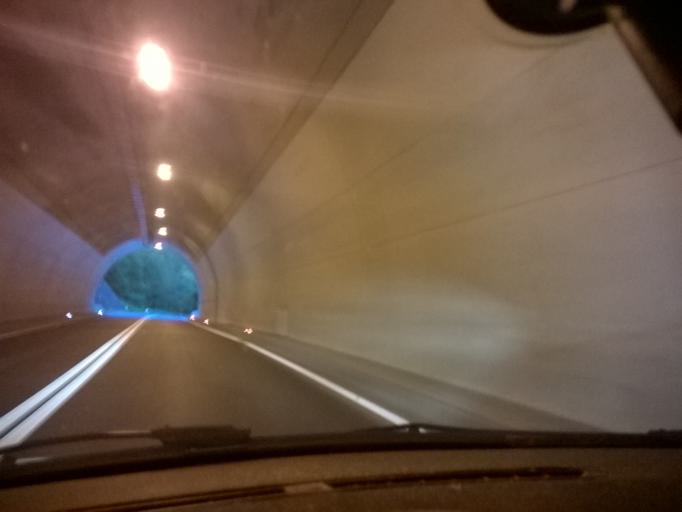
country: SI
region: Zetale
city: Zetale
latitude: 46.2481
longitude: 15.8505
